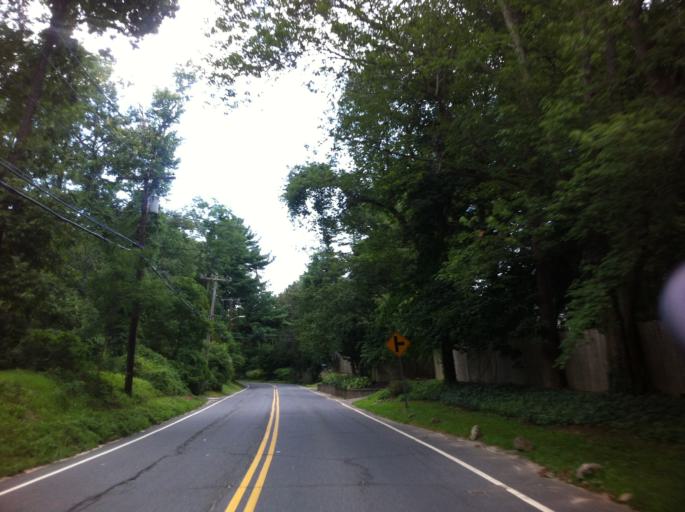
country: US
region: New York
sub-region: Nassau County
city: Old Brookville
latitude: 40.8356
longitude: -73.6008
